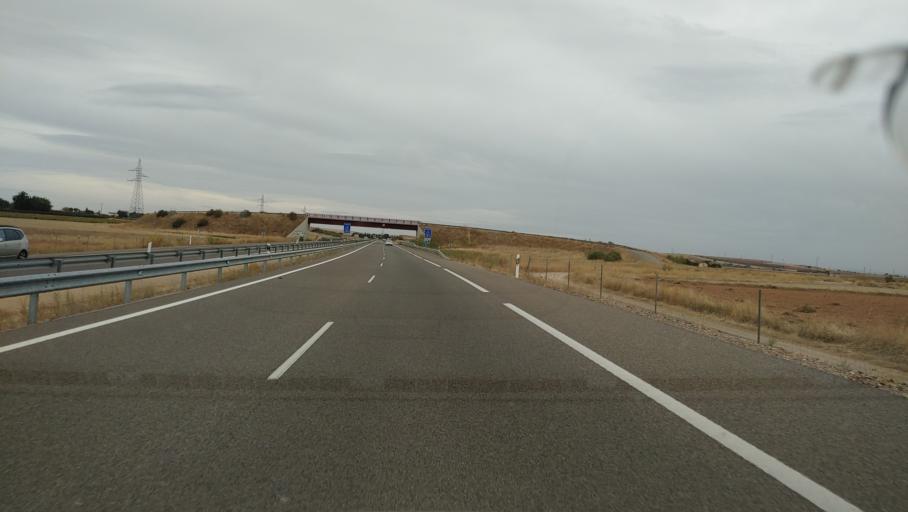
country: ES
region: Castille-La Mancha
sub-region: Provincia de Ciudad Real
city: Miguelturra
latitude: 38.9500
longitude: -3.9030
